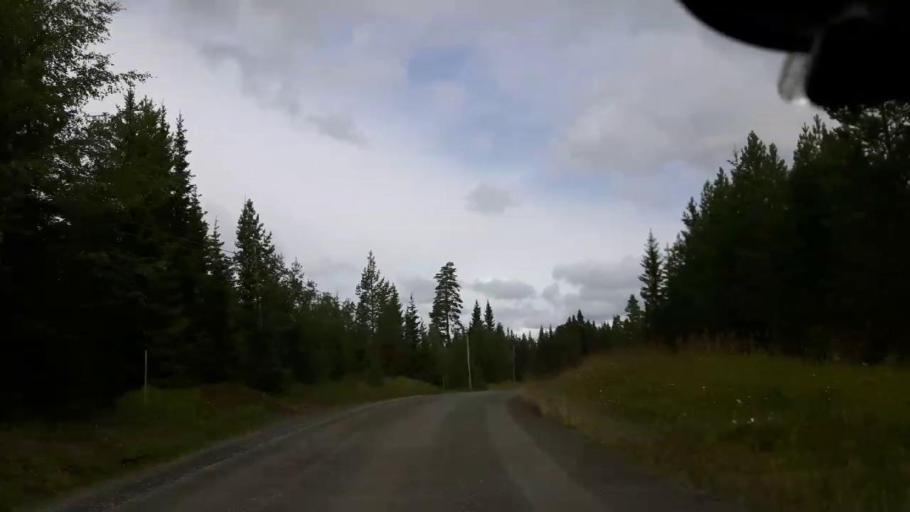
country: SE
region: Jaemtland
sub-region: Krokoms Kommun
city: Valla
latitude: 63.4184
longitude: 14.0802
